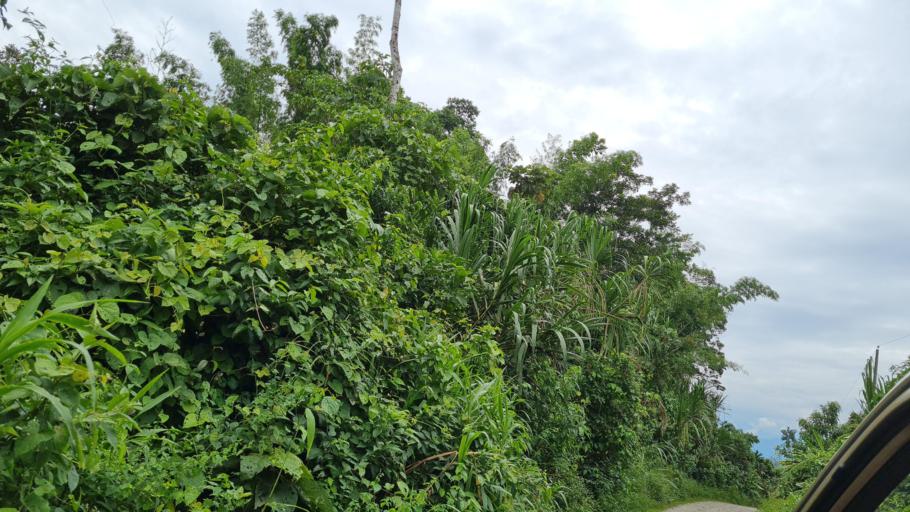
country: EC
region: Napo
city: Tena
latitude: -0.9996
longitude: -77.7593
